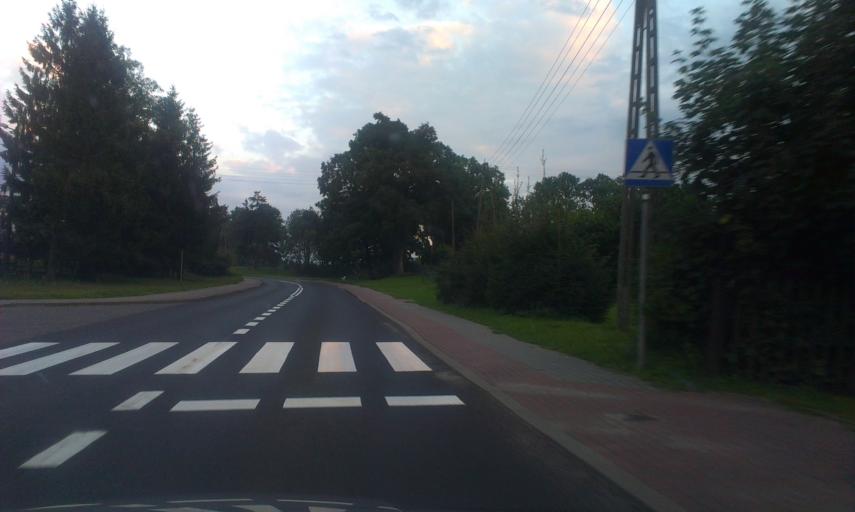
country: PL
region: West Pomeranian Voivodeship
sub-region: Powiat koszalinski
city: Bobolice
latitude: 54.0296
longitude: 16.4633
